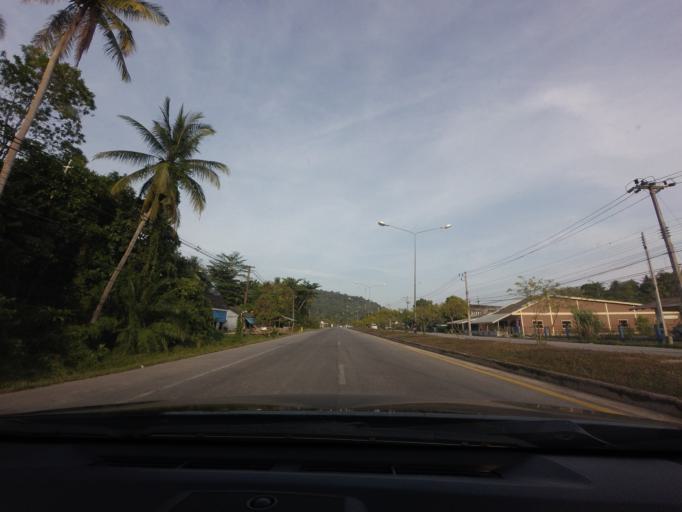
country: TH
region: Narathiwat
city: Narathiwat
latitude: 6.4172
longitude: 101.8473
